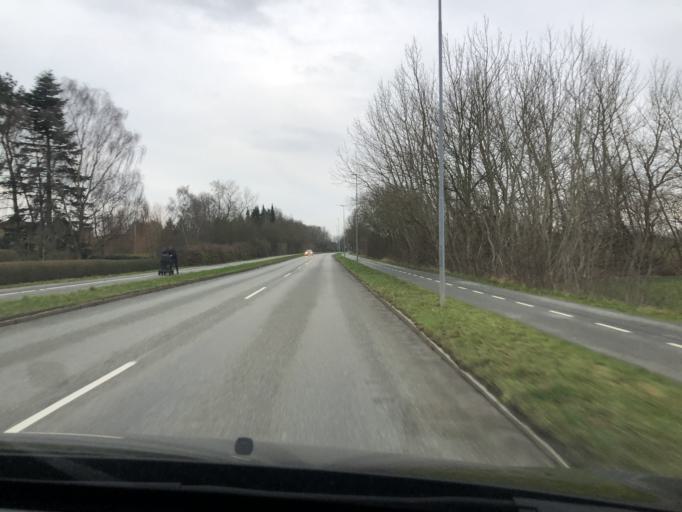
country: DK
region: South Denmark
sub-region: Svendborg Kommune
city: Svendborg
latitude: 55.0859
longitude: 10.6169
